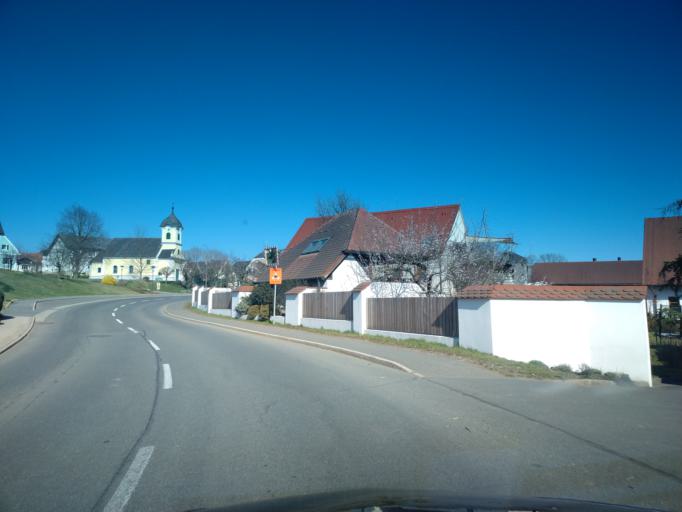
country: AT
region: Styria
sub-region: Politischer Bezirk Leibnitz
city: Weitendorf
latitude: 46.8969
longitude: 15.4652
